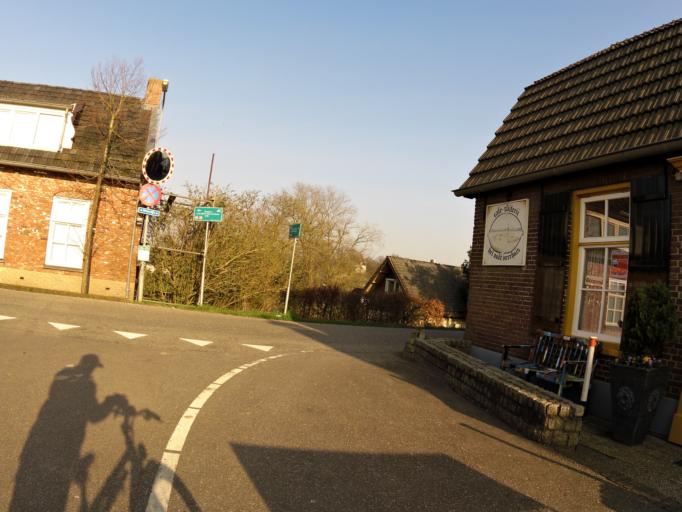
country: NL
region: North Brabant
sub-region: Gemeente Aalburg
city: Aalburg
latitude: 51.7823
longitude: 5.1224
